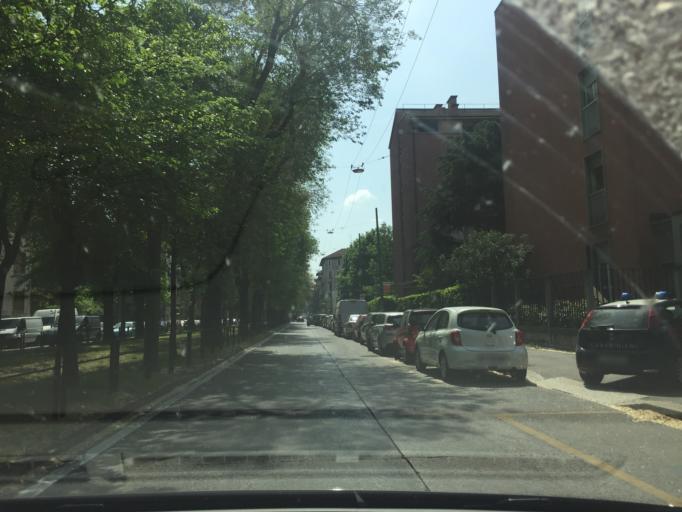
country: IT
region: Lombardy
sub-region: Citta metropolitana di Milano
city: Novate Milanese
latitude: 45.4988
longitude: 9.1514
